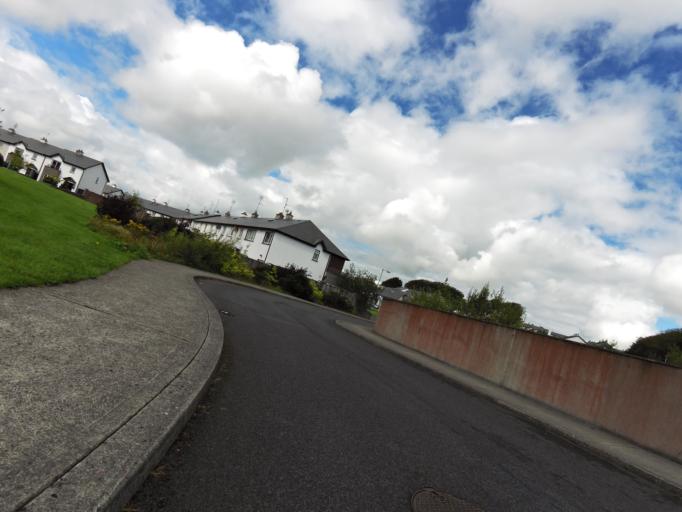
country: IE
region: Connaught
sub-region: County Galway
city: Loughrea
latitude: 53.1946
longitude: -8.5545
